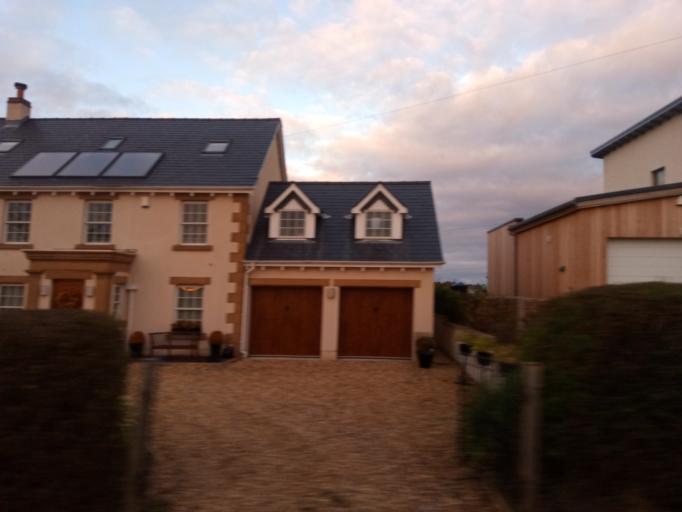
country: GB
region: Scotland
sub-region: Midlothian
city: Dalkeith
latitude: 55.8869
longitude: -3.0318
